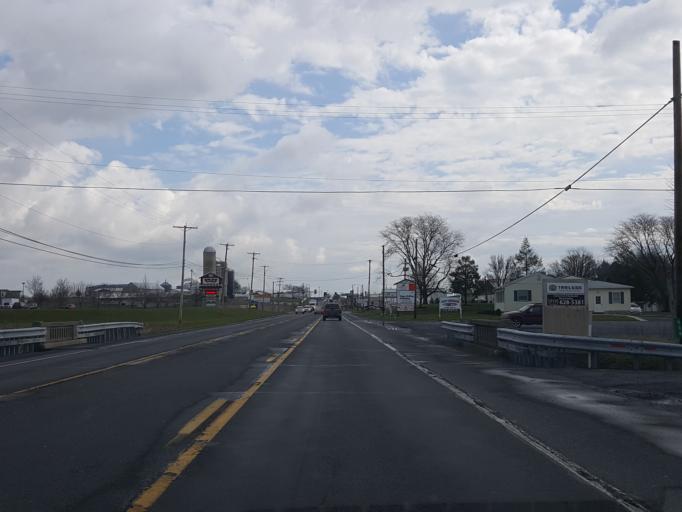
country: US
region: Pennsylvania
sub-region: Lebanon County
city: Myerstown
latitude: 40.3823
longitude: -76.2915
